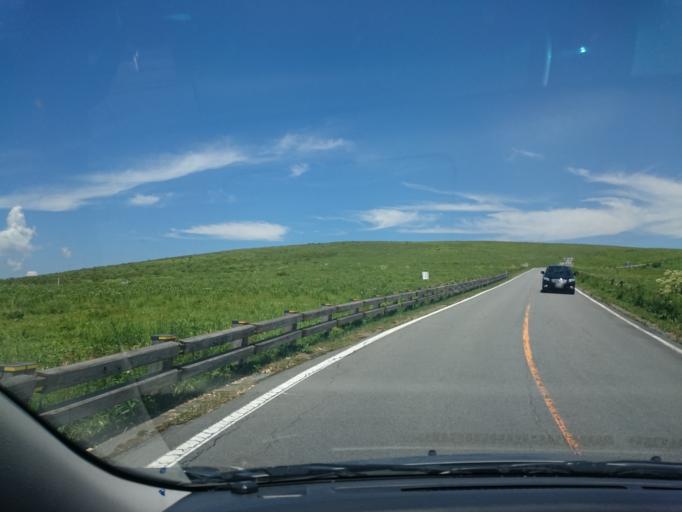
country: JP
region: Nagano
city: Suwa
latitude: 36.0995
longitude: 138.1816
